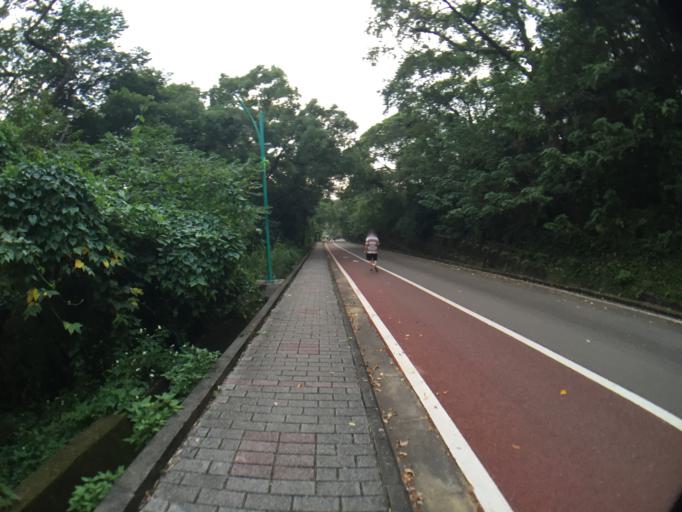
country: TW
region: Taiwan
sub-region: Hsinchu
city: Hsinchu
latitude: 24.7737
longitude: 120.9752
